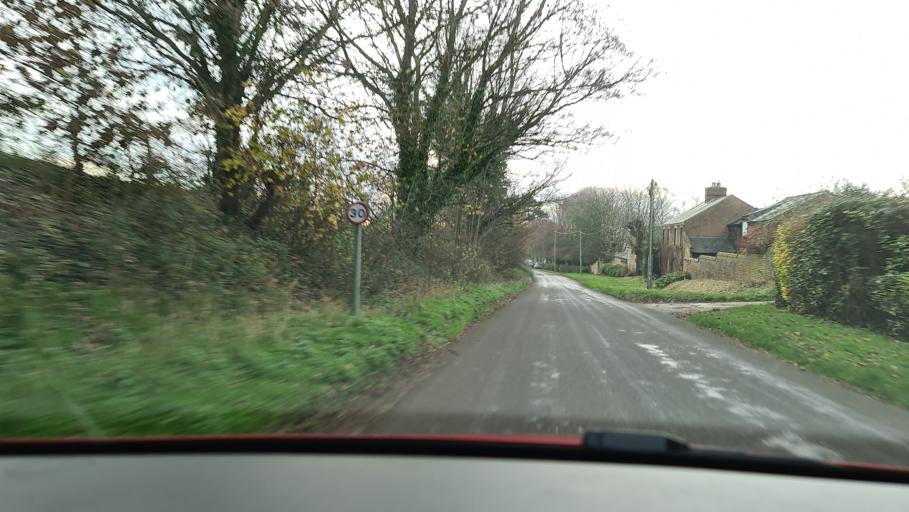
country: GB
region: England
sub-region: Buckinghamshire
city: Long Crendon
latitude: 51.7927
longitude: -0.9663
